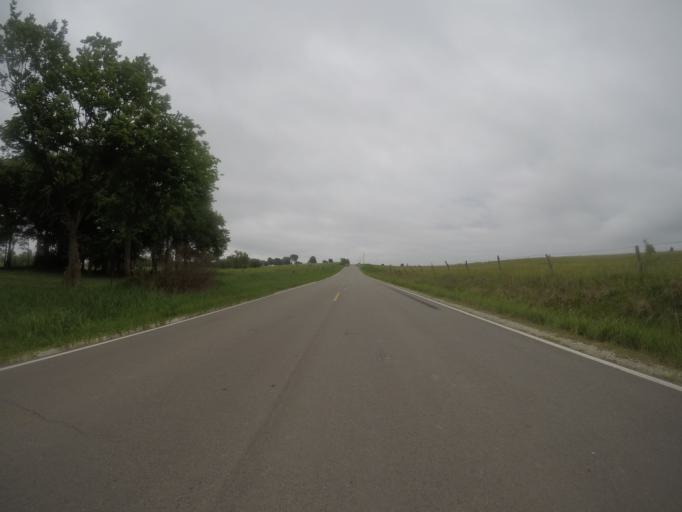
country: US
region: Kansas
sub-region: Pottawatomie County
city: Westmoreland
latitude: 39.5078
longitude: -96.1835
